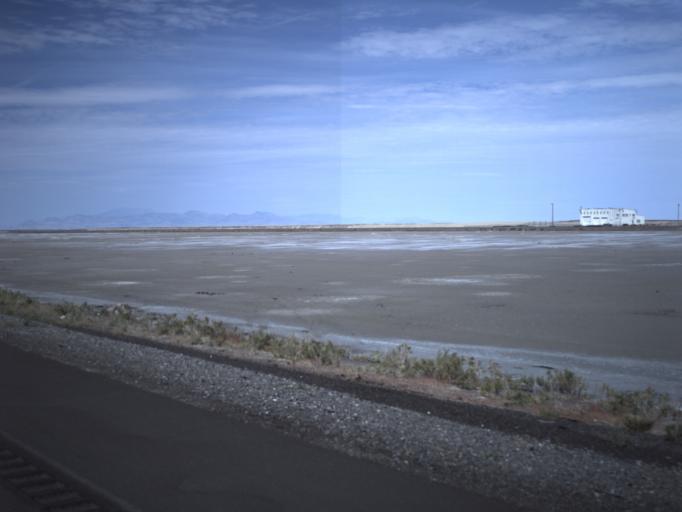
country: US
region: Utah
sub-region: Tooele County
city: Wendover
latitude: 40.7278
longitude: -113.2908
